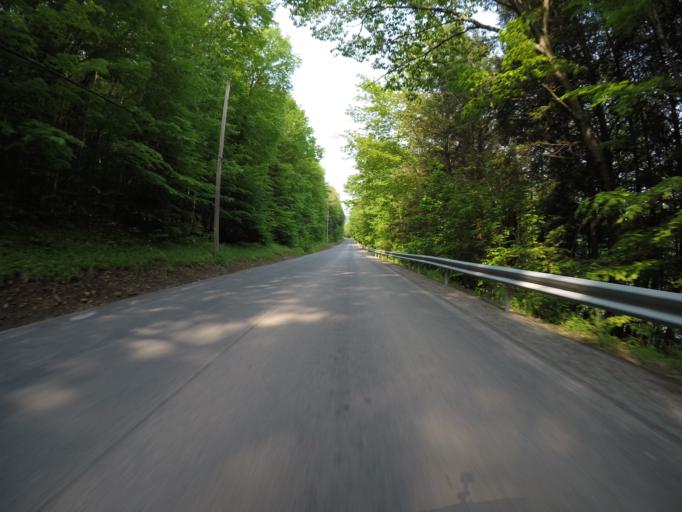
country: US
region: New York
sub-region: Sullivan County
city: Livingston Manor
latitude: 42.1145
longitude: -74.7264
